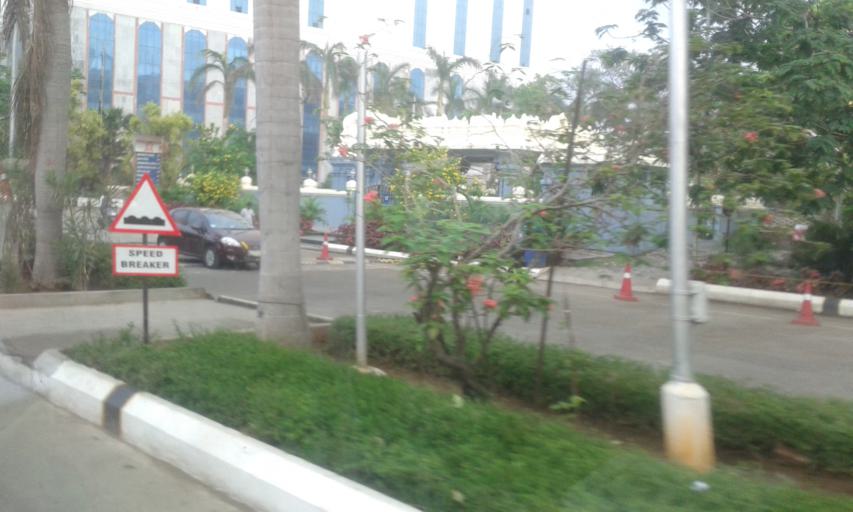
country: IN
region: Tamil Nadu
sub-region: Kancheepuram
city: Guduvancheri
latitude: 12.8229
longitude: 80.0433
